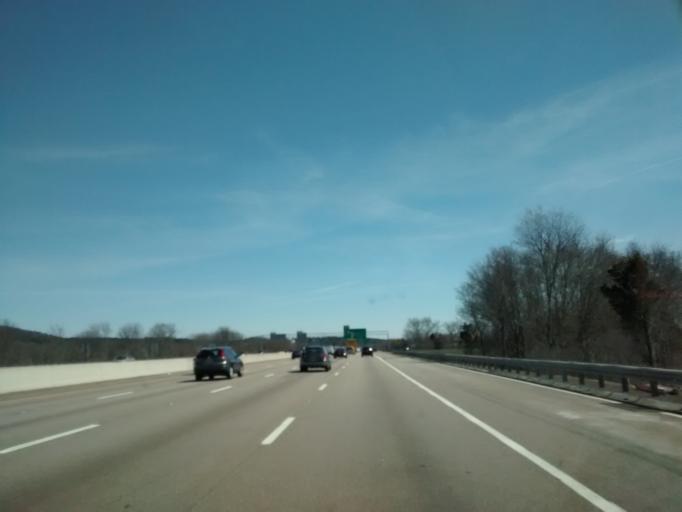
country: US
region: Massachusetts
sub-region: Norfolk County
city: Dedham
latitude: 42.2144
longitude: -71.1525
